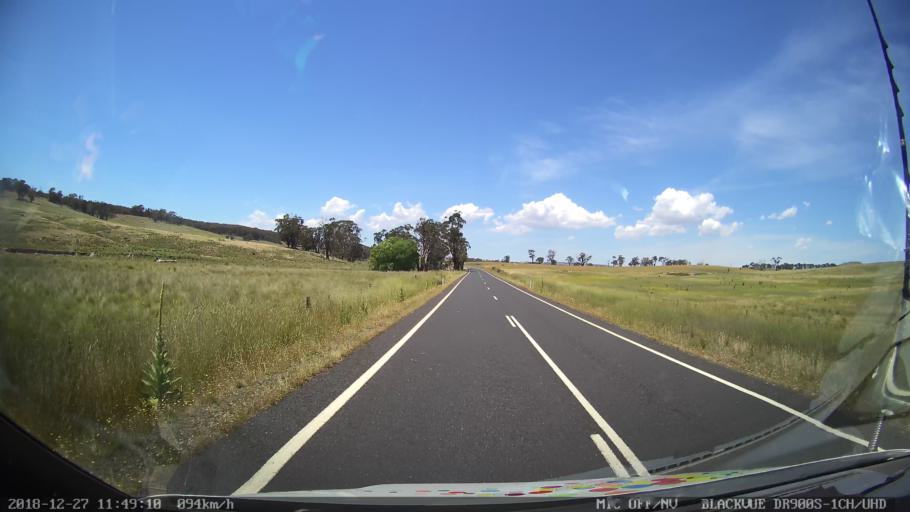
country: AU
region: New South Wales
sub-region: Bathurst Regional
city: Perthville
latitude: -33.6153
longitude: 149.4352
